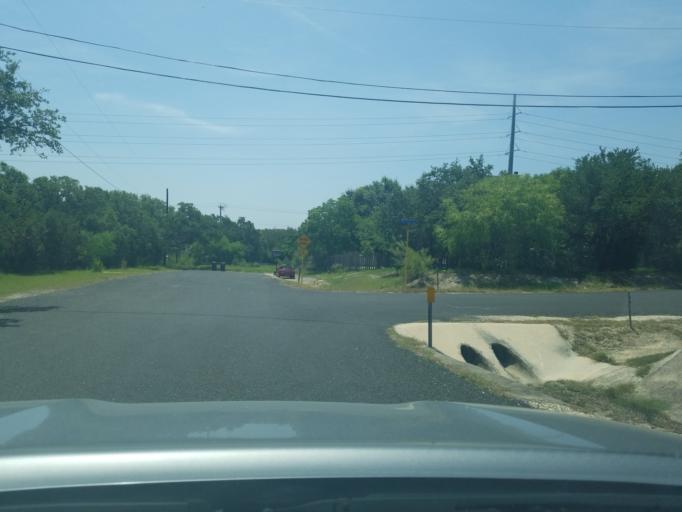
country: US
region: Texas
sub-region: Bexar County
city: Timberwood Park
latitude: 29.6712
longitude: -98.5065
